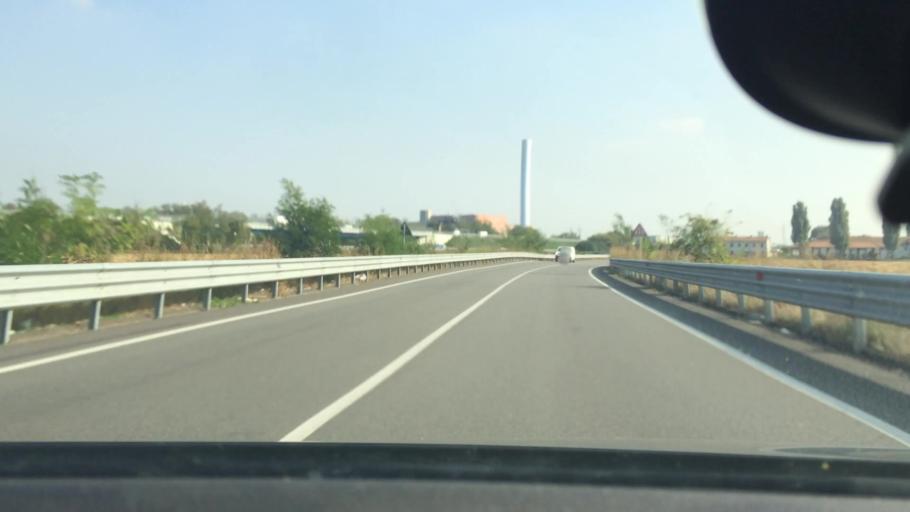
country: IT
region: Lombardy
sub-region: Citta metropolitana di Milano
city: Rho
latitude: 45.5093
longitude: 9.0600
